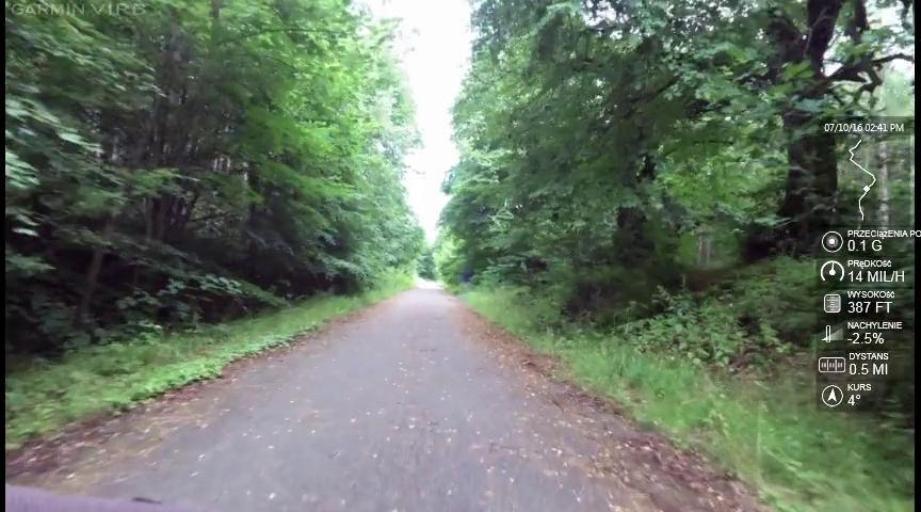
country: PL
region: West Pomeranian Voivodeship
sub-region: Powiat gryfinski
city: Banie
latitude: 53.0838
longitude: 14.6378
